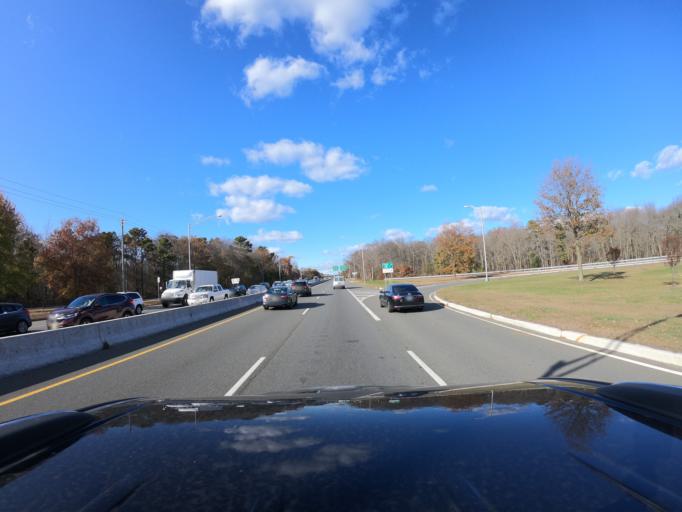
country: US
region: New Jersey
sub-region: Ocean County
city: Lakewood
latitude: 40.1606
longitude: -74.2328
